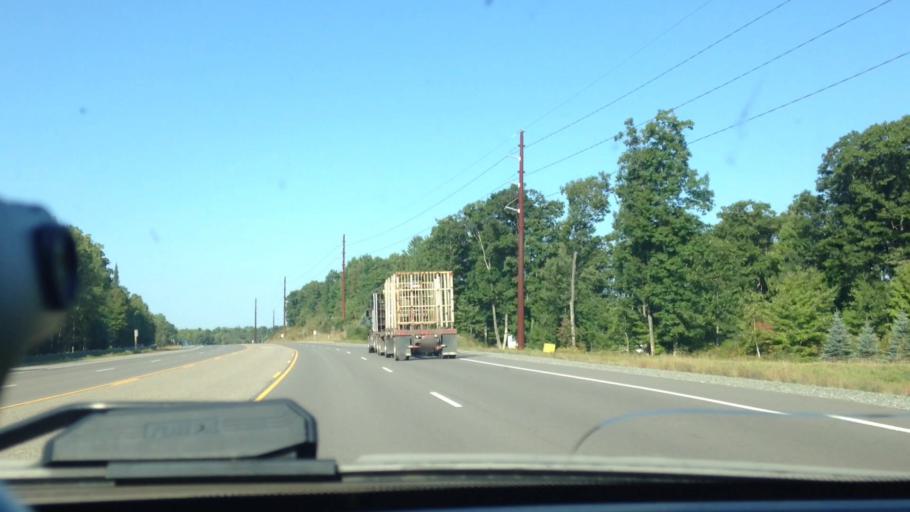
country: US
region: Michigan
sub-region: Dickinson County
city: Iron Mountain
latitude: 45.8821
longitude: -88.1324
